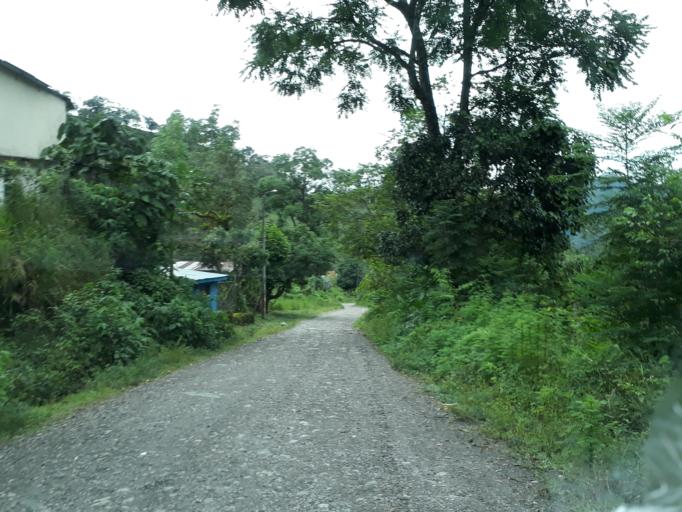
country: CO
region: Boyaca
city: Santa Maria
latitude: 4.7518
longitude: -73.3265
